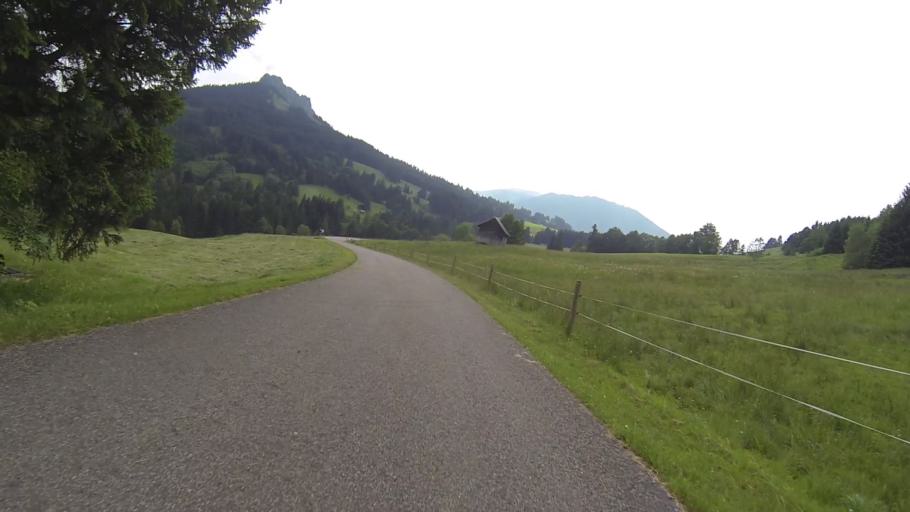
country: AT
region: Tyrol
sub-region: Politischer Bezirk Reutte
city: Jungholz
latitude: 47.5738
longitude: 10.4680
